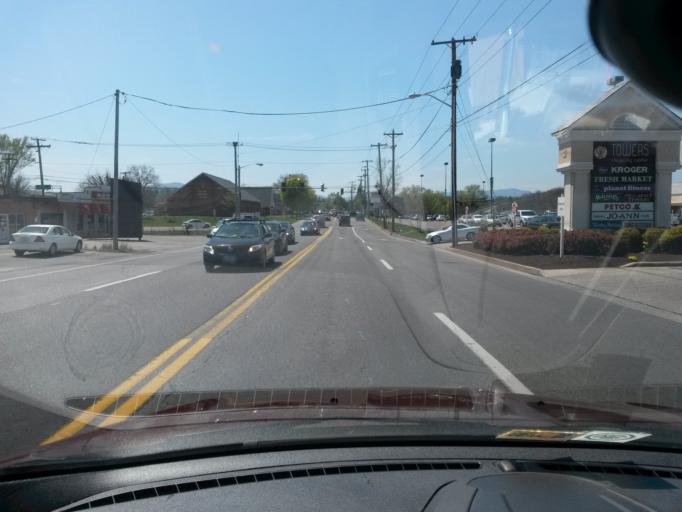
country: US
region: Virginia
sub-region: City of Roanoke
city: Roanoke
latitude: 37.2548
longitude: -79.9561
